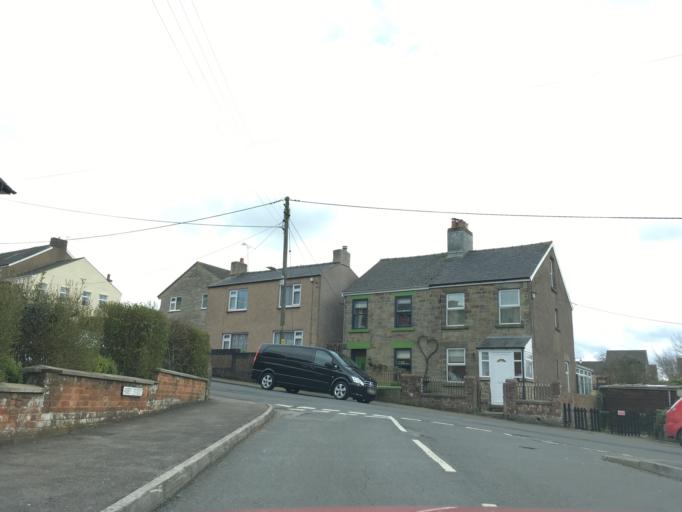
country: GB
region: England
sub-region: Gloucestershire
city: Cinderford
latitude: 51.8203
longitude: -2.4963
